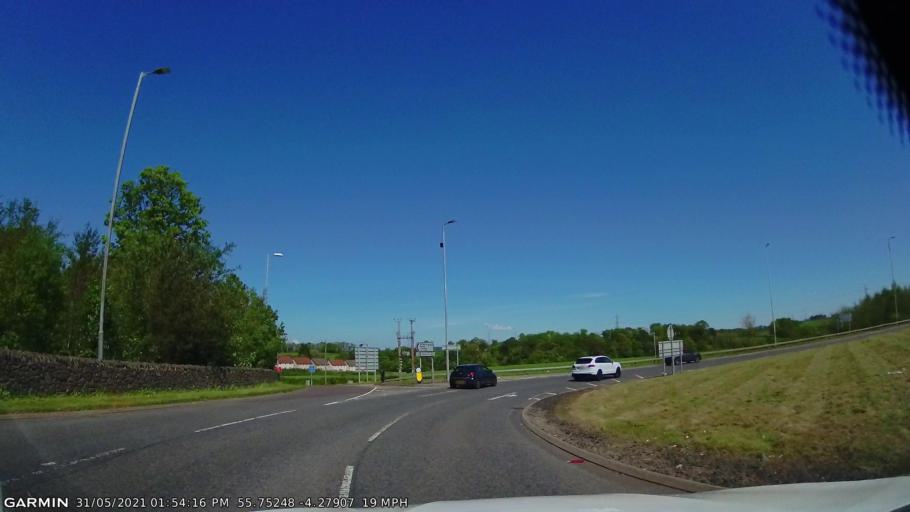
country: GB
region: Scotland
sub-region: East Renfrewshire
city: Eaglesham
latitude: 55.7523
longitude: -4.2791
